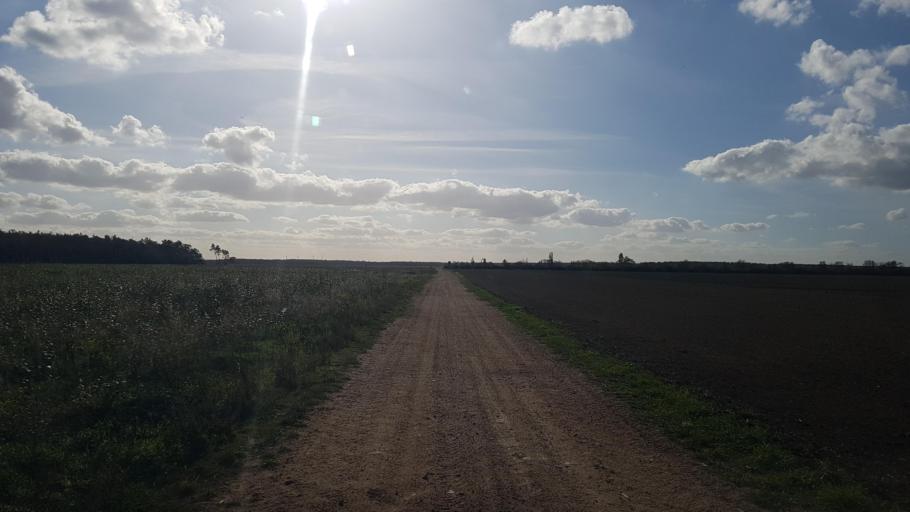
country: DE
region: Saxony
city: Nauwalde
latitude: 51.4518
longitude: 13.3290
